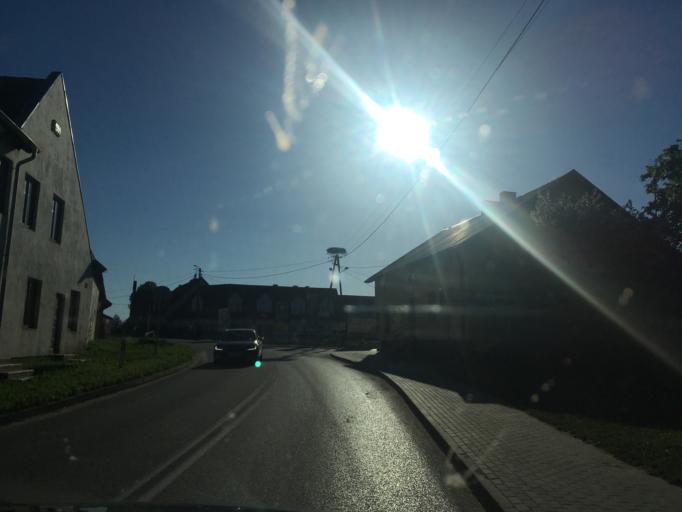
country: PL
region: Warmian-Masurian Voivodeship
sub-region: Powiat piski
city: Ruciane-Nida
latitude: 53.6886
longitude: 21.4972
